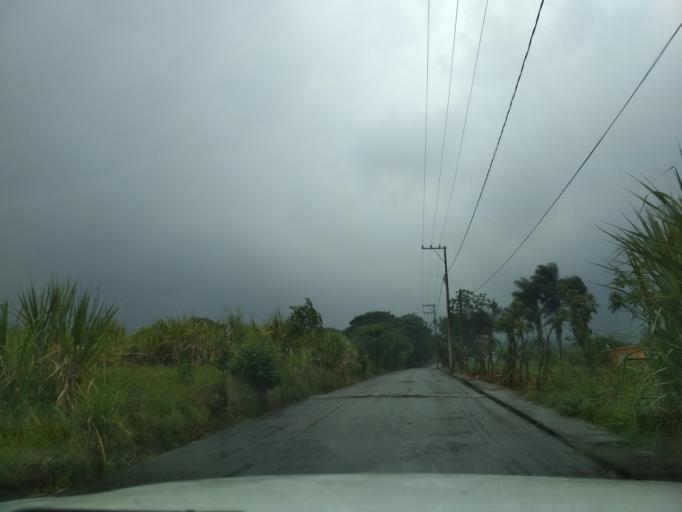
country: MX
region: Veracruz
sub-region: Mariano Escobedo
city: Chicola
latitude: 18.8995
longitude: -97.1180
